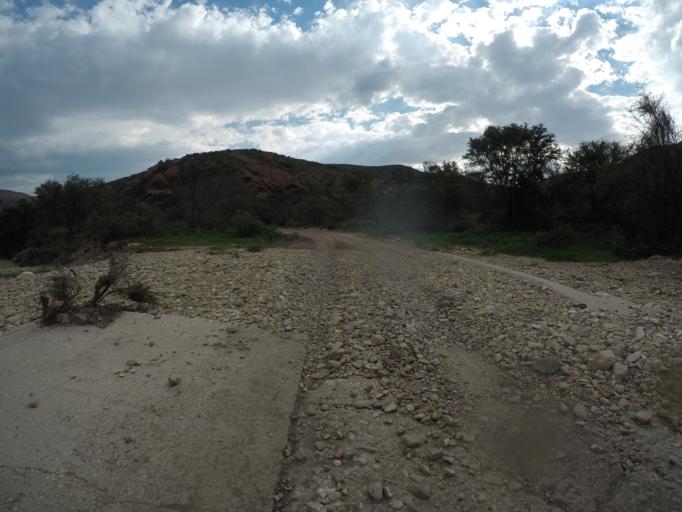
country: ZA
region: Eastern Cape
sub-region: Cacadu District Municipality
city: Kareedouw
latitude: -33.6003
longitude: 24.2087
